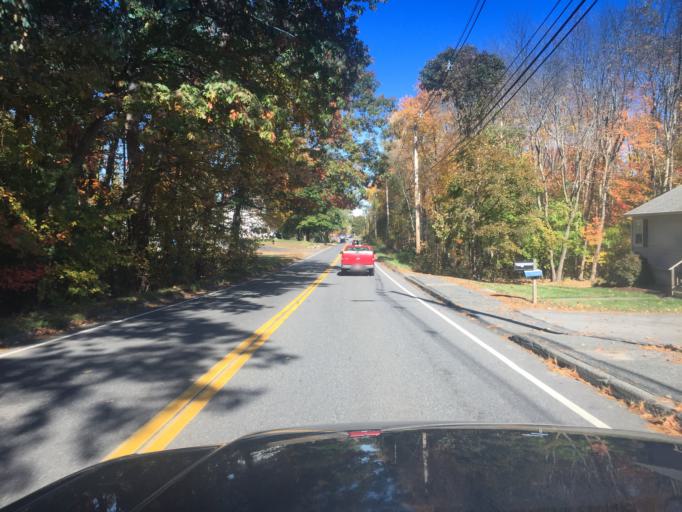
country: US
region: Massachusetts
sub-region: Middlesex County
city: Hudson
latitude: 42.3911
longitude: -71.5417
